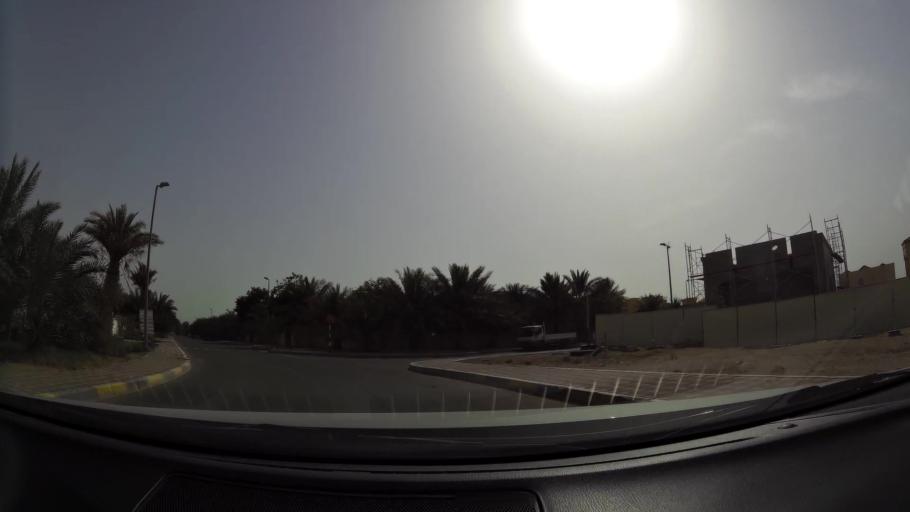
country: AE
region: Abu Dhabi
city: Al Ain
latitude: 24.1455
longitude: 55.7046
